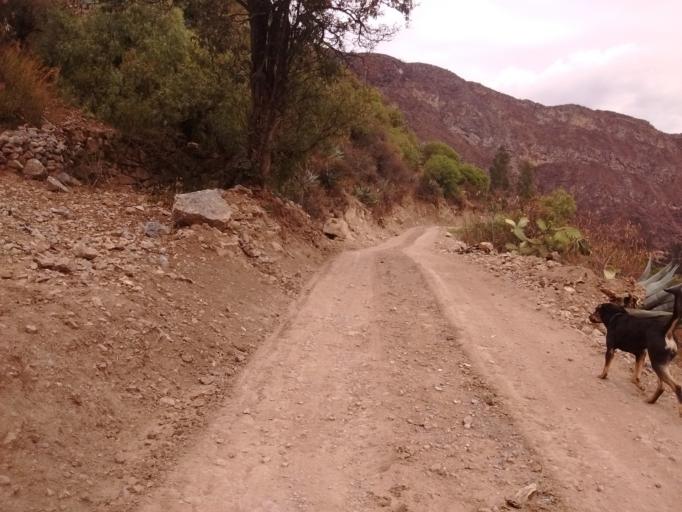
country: PE
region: Ayacucho
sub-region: Provincia de Victor Fajardo
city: Canaria
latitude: -13.8789
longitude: -73.9360
